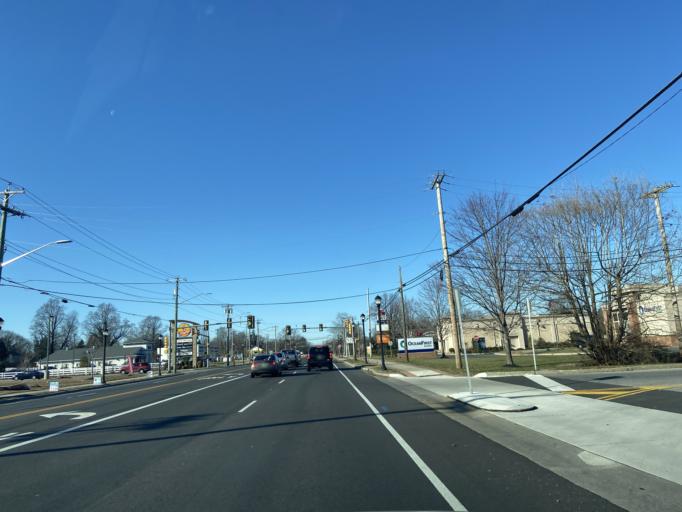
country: US
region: New Jersey
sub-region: Cumberland County
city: Vineland
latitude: 39.4876
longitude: -75.0474
